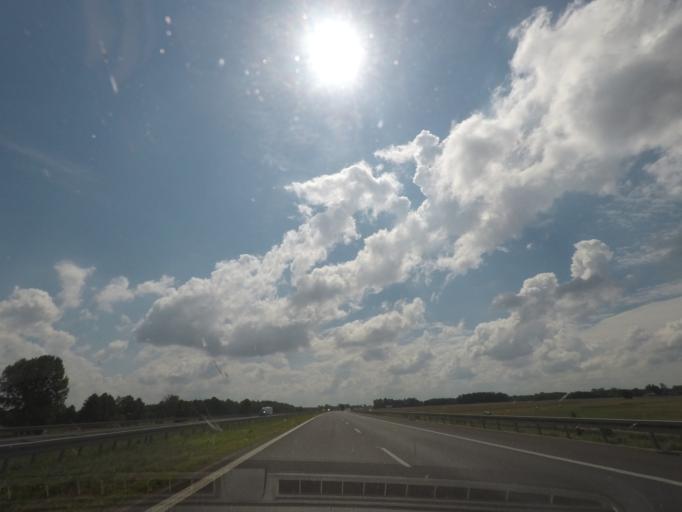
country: PL
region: Lodz Voivodeship
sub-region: Powiat zgierski
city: Strykow
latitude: 51.9494
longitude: 19.6049
